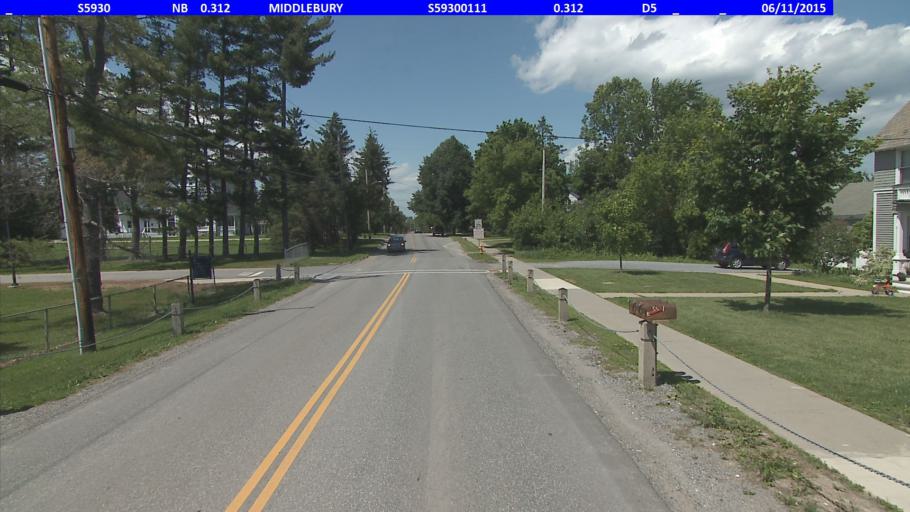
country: US
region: Vermont
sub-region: Addison County
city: Middlebury (village)
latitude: 44.0049
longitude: -73.1701
